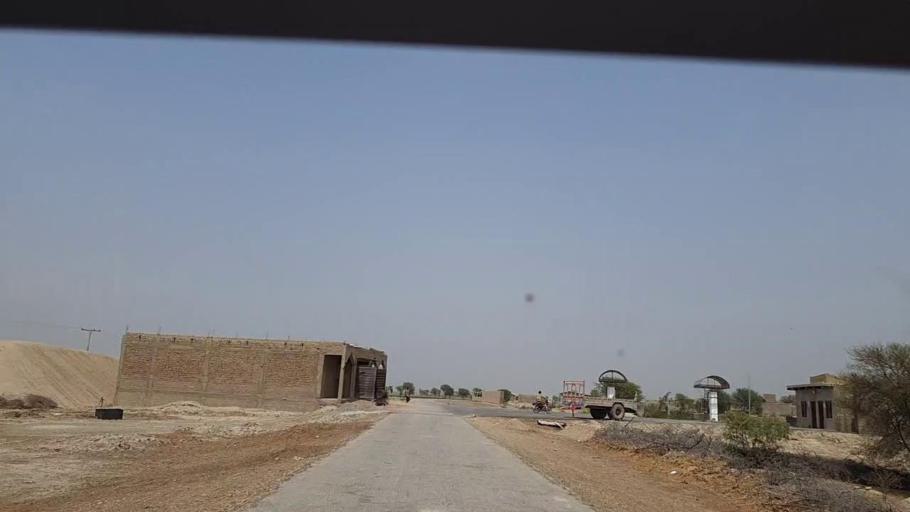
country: PK
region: Sindh
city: Khairpur Nathan Shah
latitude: 27.0241
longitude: 67.5901
